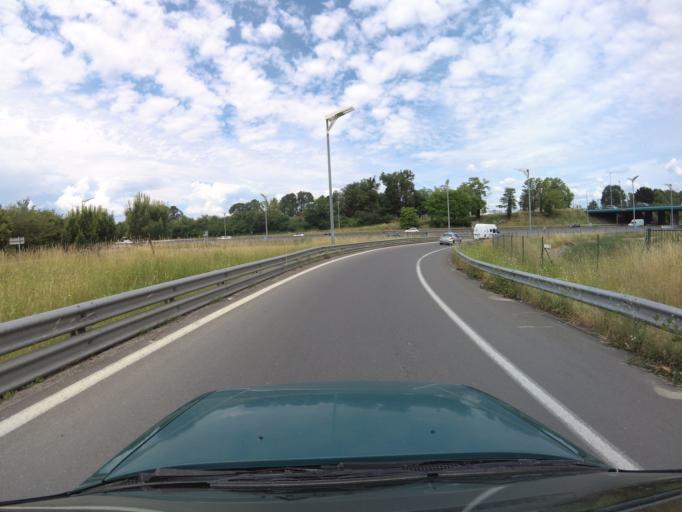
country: FR
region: Aquitaine
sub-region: Departement de la Gironde
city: Gradignan
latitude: 44.7890
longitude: -0.6065
